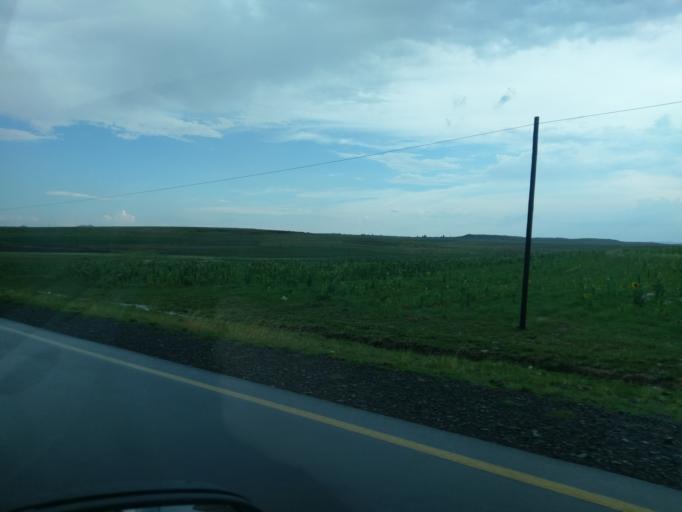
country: LS
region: Mafeteng
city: Mafeteng
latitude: -29.7844
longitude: 27.2029
